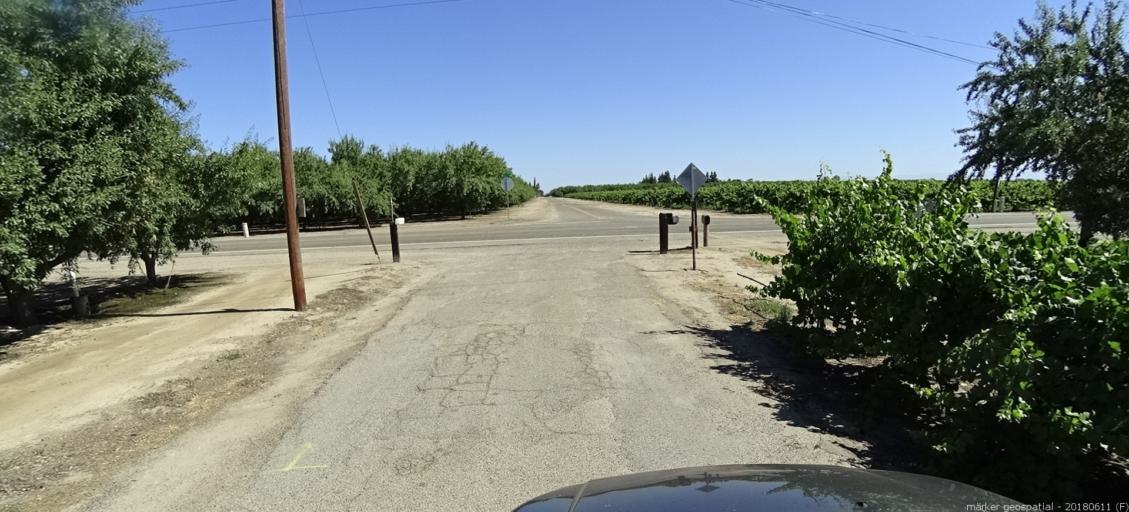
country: US
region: California
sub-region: Madera County
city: Madera
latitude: 36.9525
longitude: -120.1749
